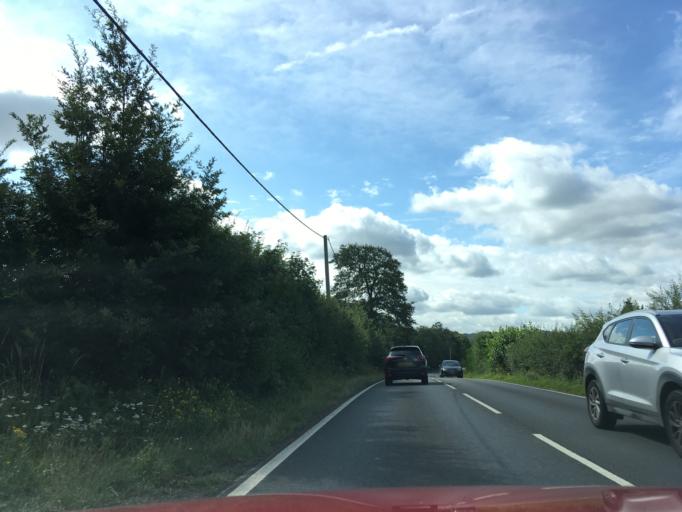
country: GB
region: England
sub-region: Kent
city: Staplehurst
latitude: 51.1487
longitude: 0.5521
